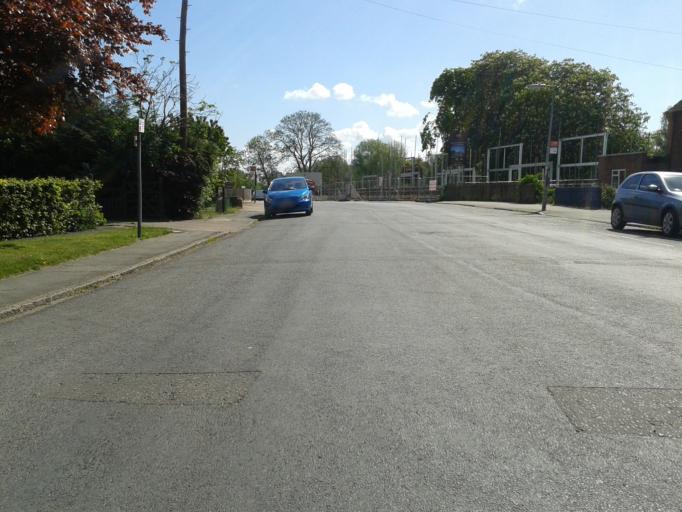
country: GB
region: England
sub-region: Cambridgeshire
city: Cambridge
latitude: 52.2185
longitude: 0.1481
